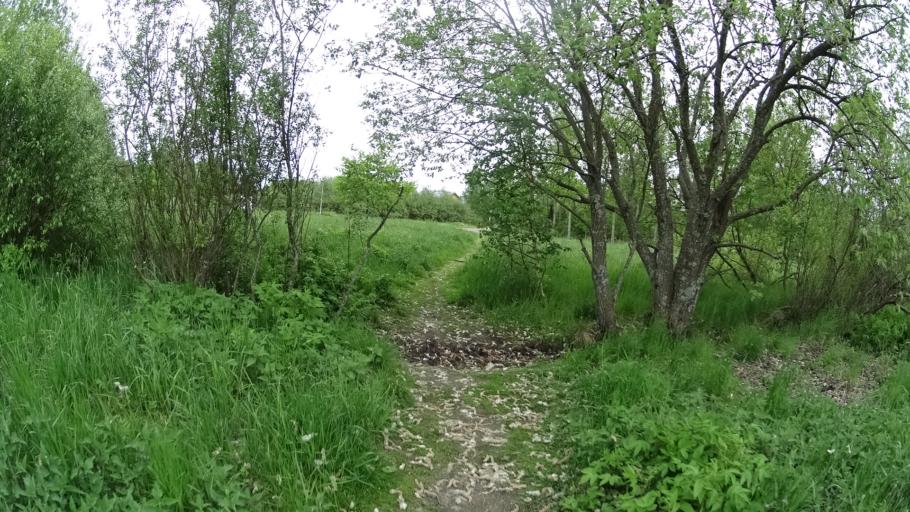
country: FI
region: Uusimaa
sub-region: Helsinki
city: Vantaa
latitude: 60.2762
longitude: 25.0586
